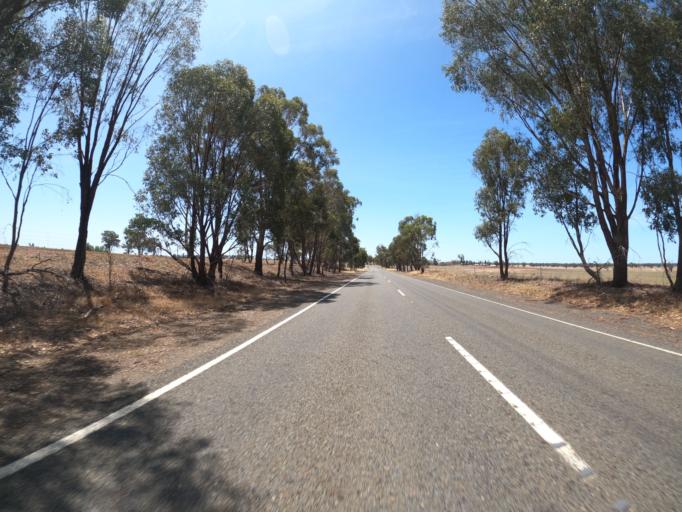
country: AU
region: Victoria
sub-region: Moira
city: Yarrawonga
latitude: -36.1018
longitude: 145.9925
